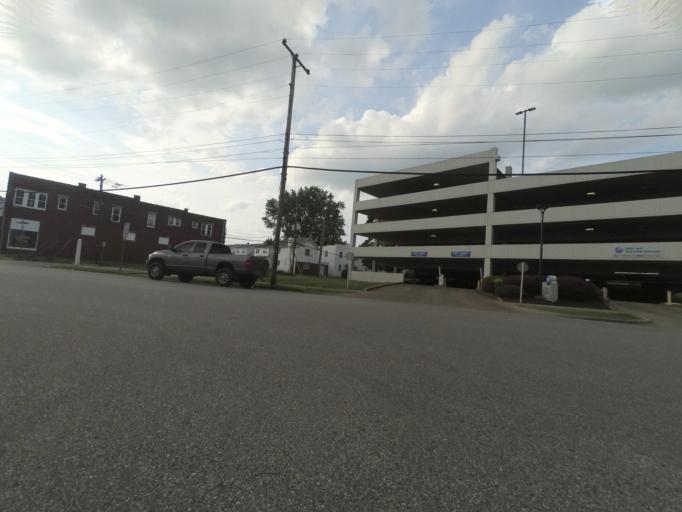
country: US
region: West Virginia
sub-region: Cabell County
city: Huntington
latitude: 38.4317
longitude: -82.4026
